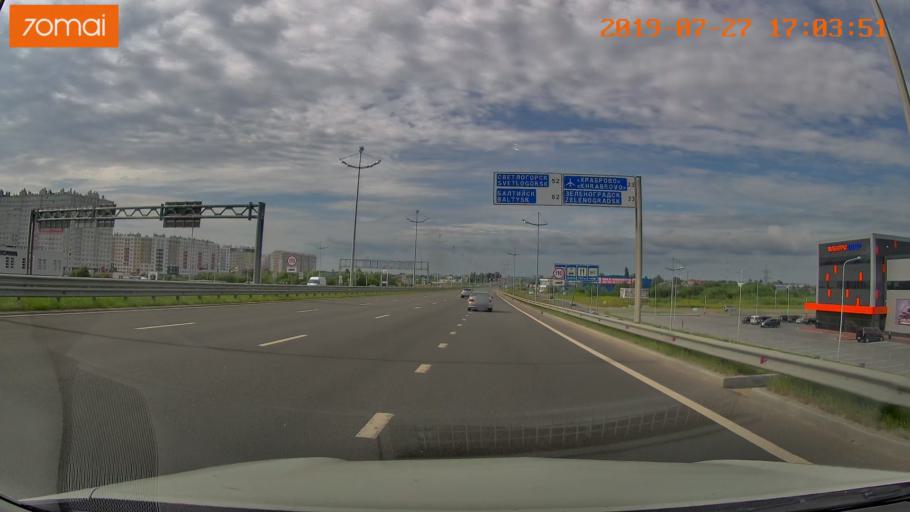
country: RU
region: Kaliningrad
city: Bol'shoe Isakovo
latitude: 54.7082
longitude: 20.5984
